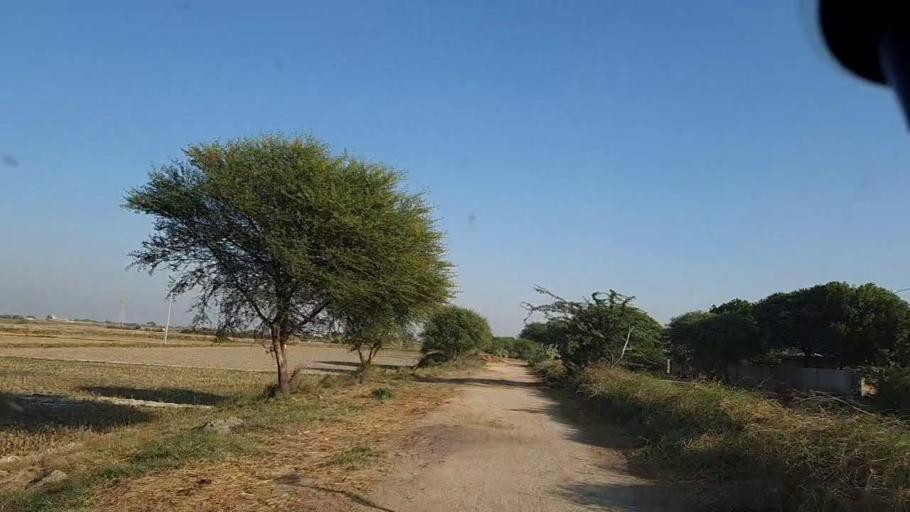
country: PK
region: Sindh
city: Chuhar Jamali
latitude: 24.5616
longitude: 68.0697
